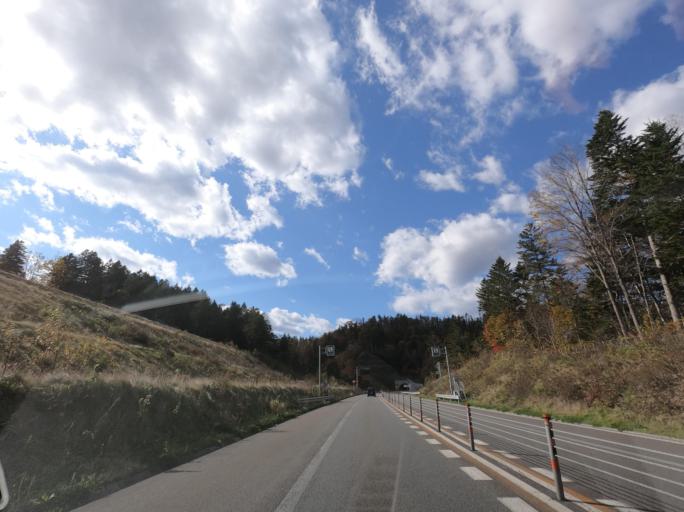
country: JP
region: Hokkaido
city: Kushiro
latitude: 43.0789
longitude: 144.0440
